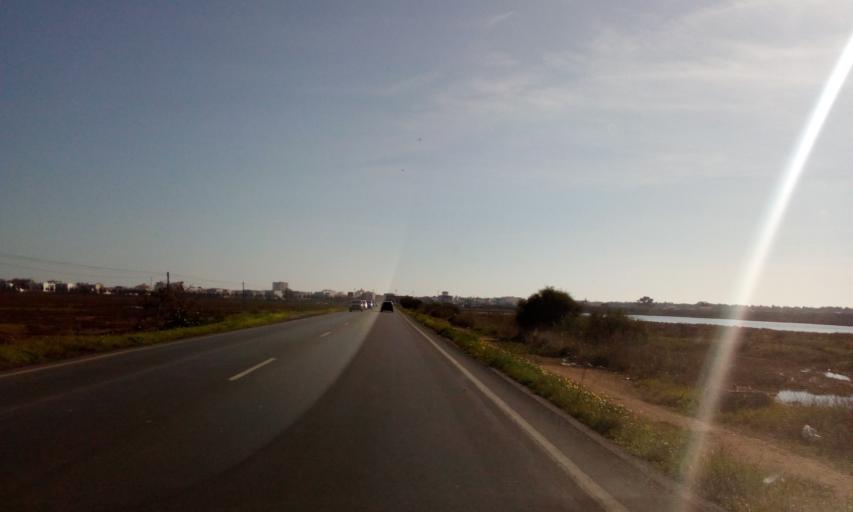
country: PT
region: Faro
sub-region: Vila Real de Santo Antonio
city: Vila Real de Santo Antonio
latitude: 37.2045
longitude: -7.4327
